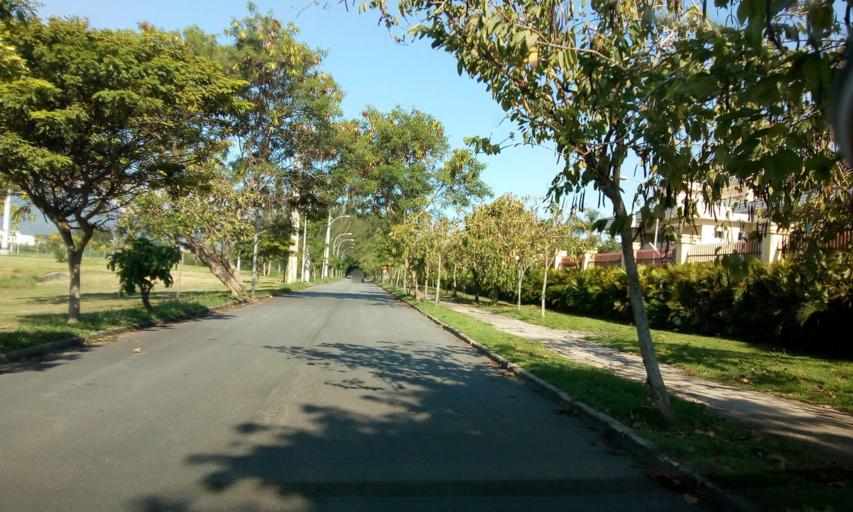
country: BR
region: Rio de Janeiro
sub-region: Nilopolis
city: Nilopolis
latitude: -22.9949
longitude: -43.3979
